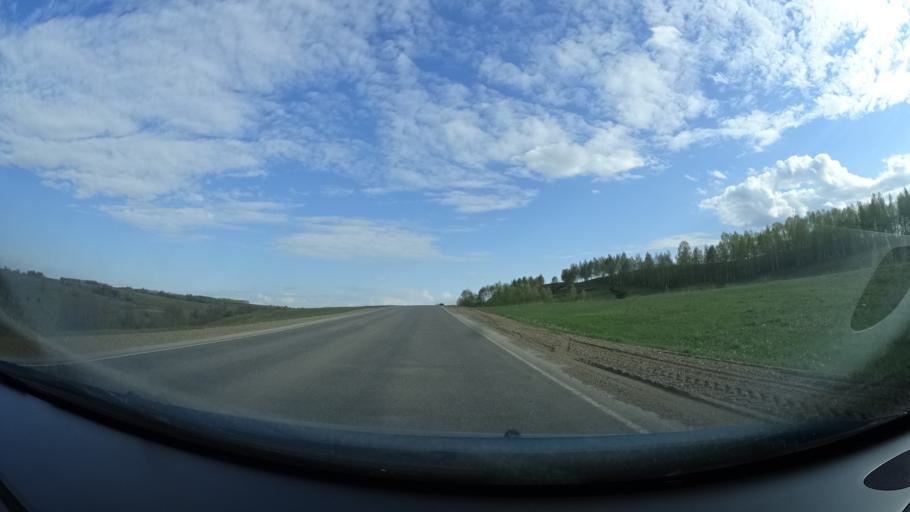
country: RU
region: Bashkortostan
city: Blagoveshchensk
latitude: 55.1148
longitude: 55.8411
